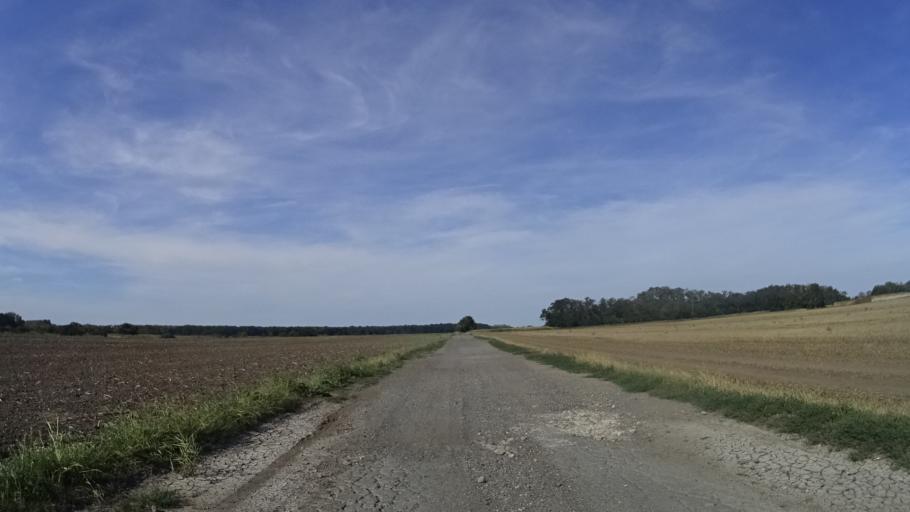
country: AT
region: Lower Austria
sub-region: Politischer Bezirk Ganserndorf
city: Durnkrut
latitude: 48.4451
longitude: 16.8800
